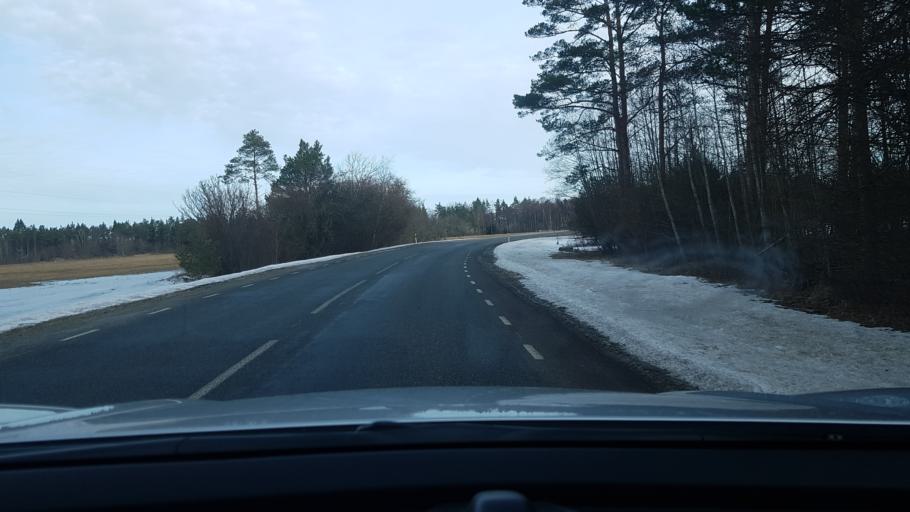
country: EE
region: Saare
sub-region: Kuressaare linn
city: Kuressaare
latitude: 58.4025
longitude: 22.6431
